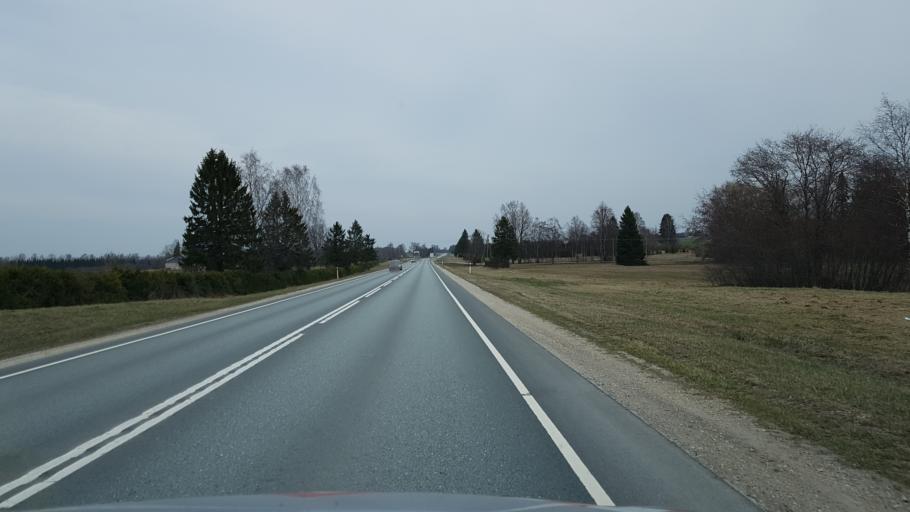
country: EE
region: Laeaene-Virumaa
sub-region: Kadrina vald
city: Kadrina
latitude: 59.3118
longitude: 26.0808
